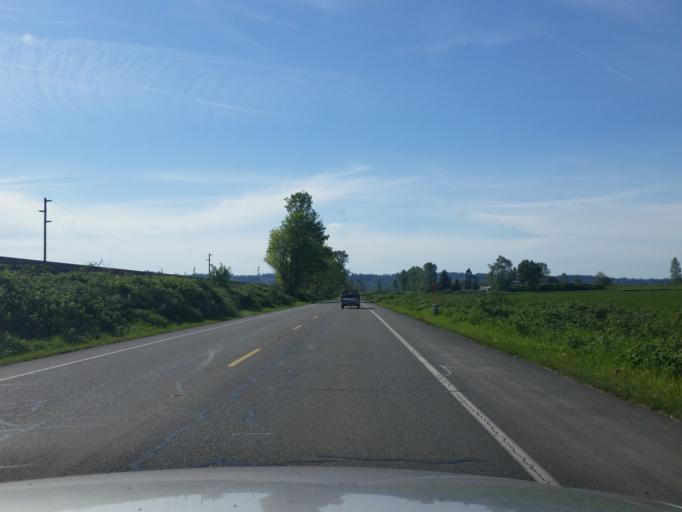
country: US
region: Washington
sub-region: Snohomish County
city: Fobes Hill
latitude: 47.9176
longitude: -122.1371
